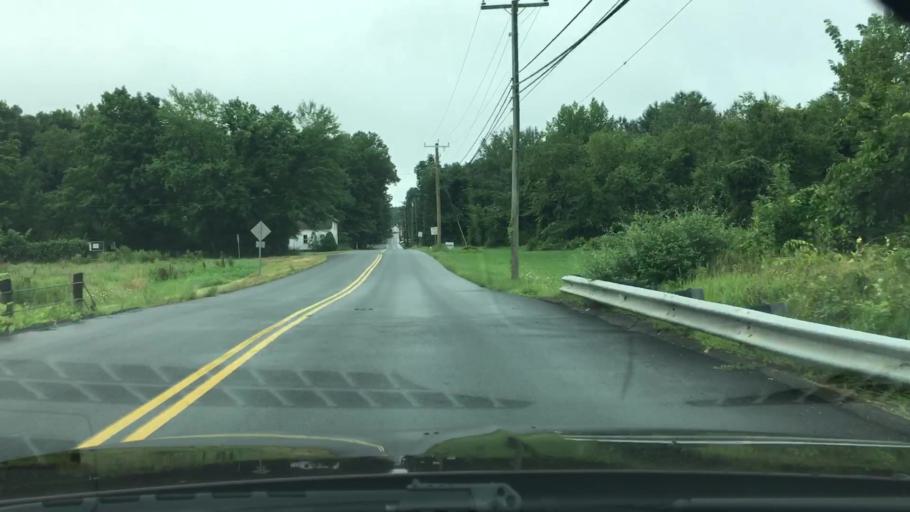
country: US
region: Connecticut
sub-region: Hartford County
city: Tariffville
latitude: 41.9140
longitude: -72.7822
